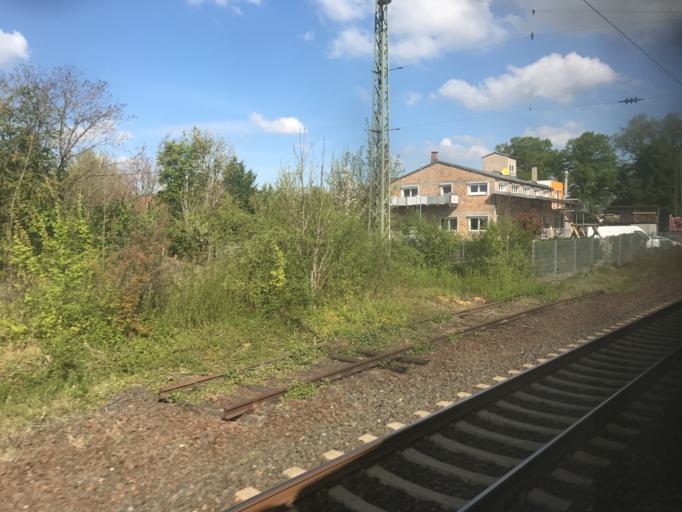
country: DE
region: Rheinland-Pfalz
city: Alsheim
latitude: 49.7664
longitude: 8.3429
